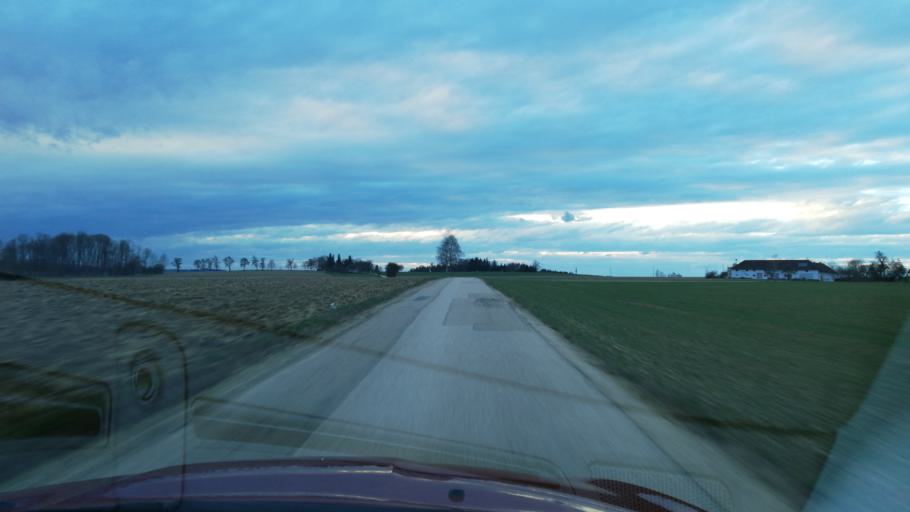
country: AT
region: Upper Austria
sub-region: Wels-Land
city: Buchkirchen
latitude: 48.2095
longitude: 14.0241
